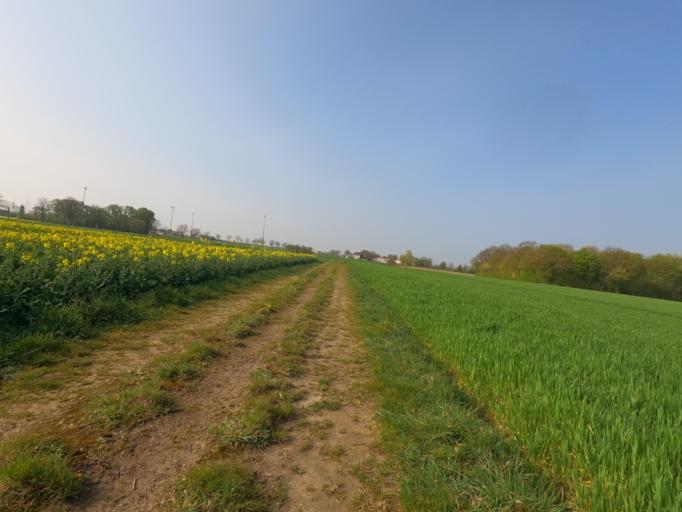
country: DE
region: North Rhine-Westphalia
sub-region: Regierungsbezirk Koln
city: Heinsberg
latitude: 51.0331
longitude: 6.1126
